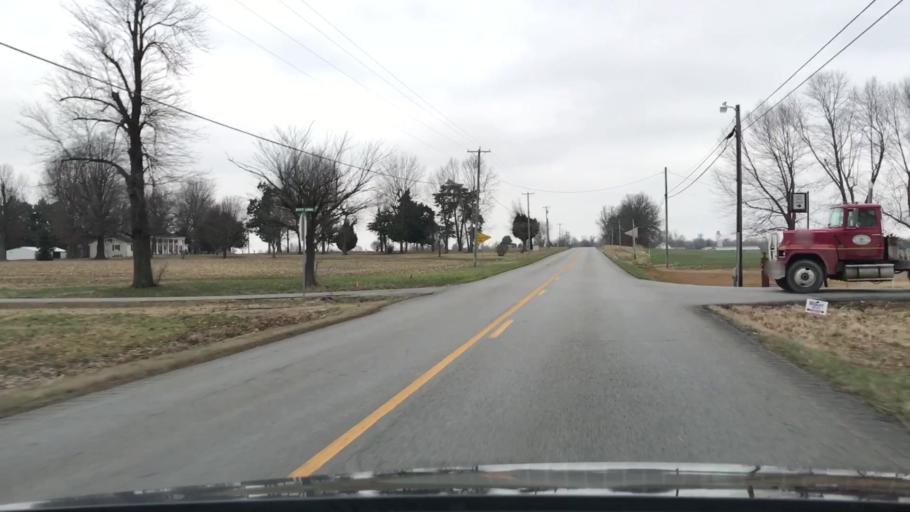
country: US
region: Kentucky
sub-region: Muhlenberg County
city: Morehead
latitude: 37.3919
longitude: -87.2552
